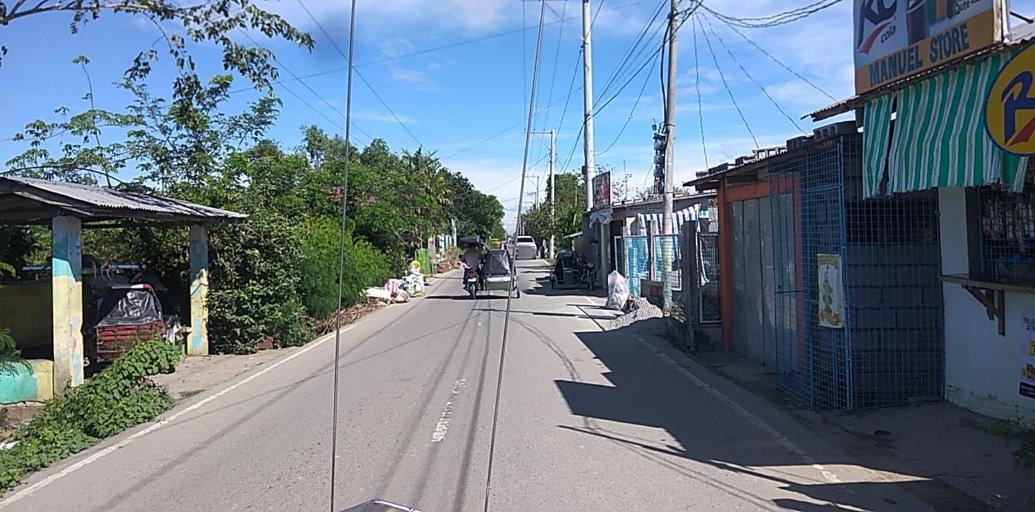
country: PH
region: Central Luzon
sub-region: Province of Pampanga
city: Candaba
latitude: 15.0875
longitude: 120.8107
